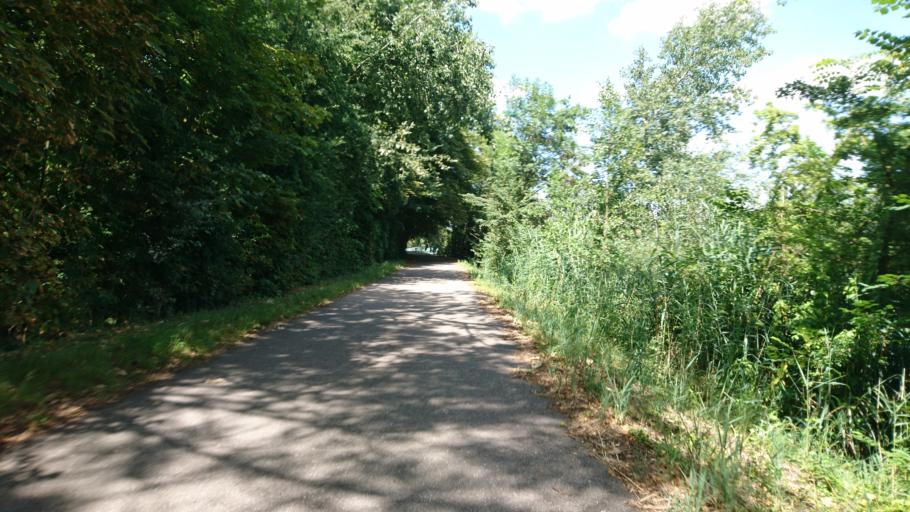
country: FR
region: Lorraine
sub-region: Departement de la Moselle
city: Longeville-les-Metz
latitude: 49.1083
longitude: 6.1419
